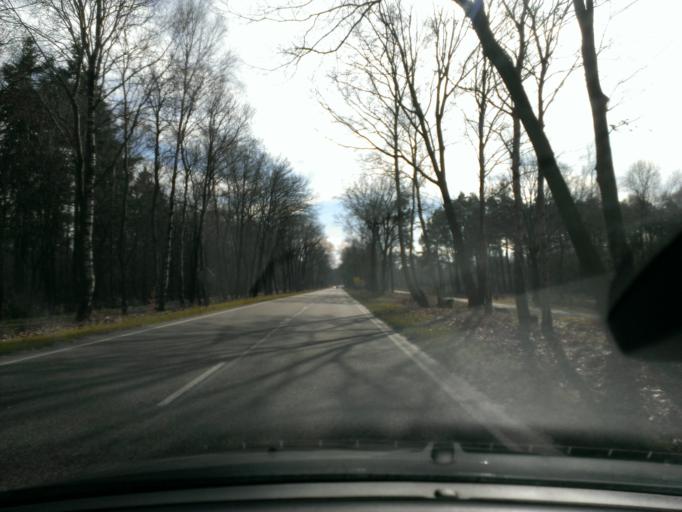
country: NL
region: Gelderland
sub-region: Gemeente Heerde
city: Heerde
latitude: 52.4351
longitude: 6.0141
